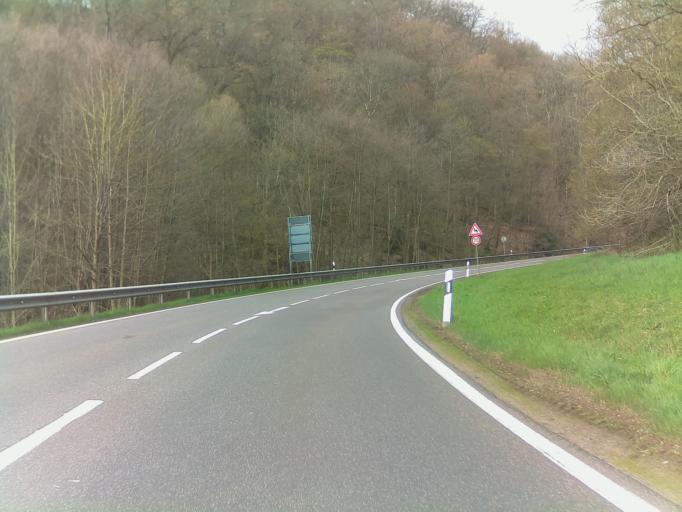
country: DE
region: Rheinland-Pfalz
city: Morschied
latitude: 49.7910
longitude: 7.3214
